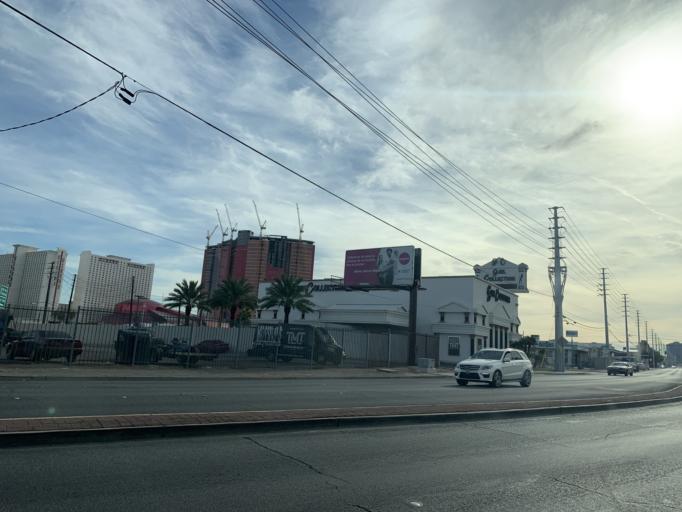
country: US
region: Nevada
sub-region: Clark County
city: Las Vegas
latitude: 36.1433
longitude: -115.1691
